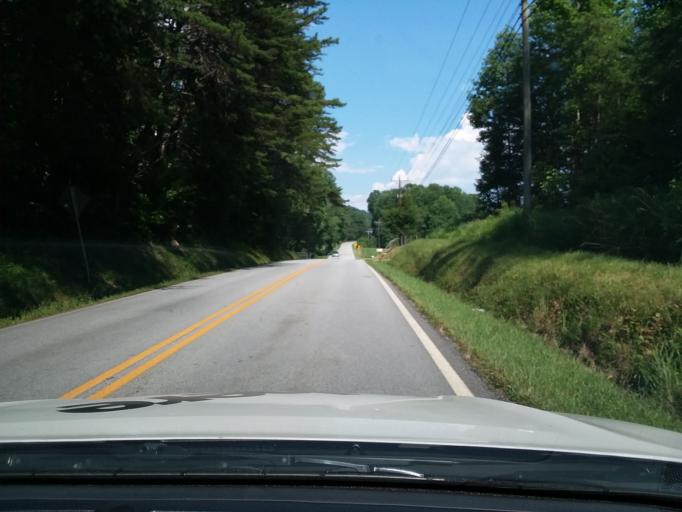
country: US
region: Georgia
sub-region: Rabun County
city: Clayton
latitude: 34.8581
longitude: -83.4625
